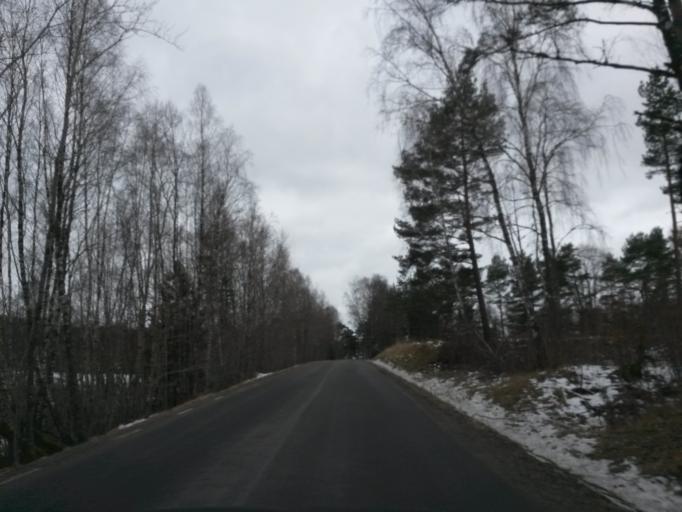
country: SE
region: Vaestra Goetaland
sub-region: Vargarda Kommun
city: Vargarda
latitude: 58.0311
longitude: 12.8421
